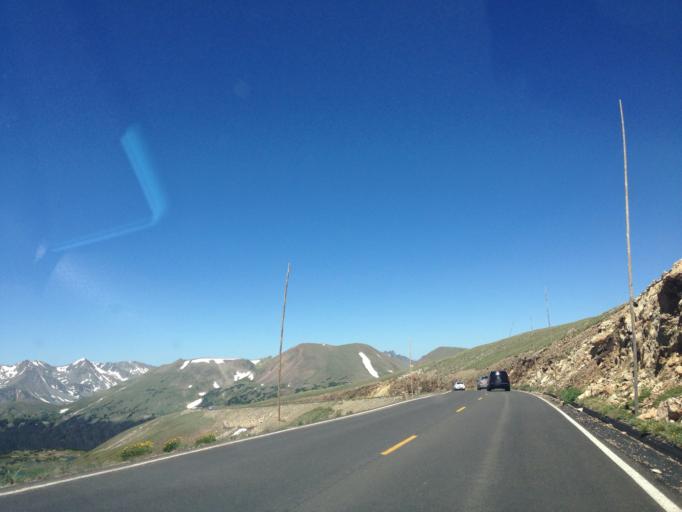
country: US
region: Colorado
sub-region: Larimer County
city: Estes Park
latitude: 40.4316
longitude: -105.7618
